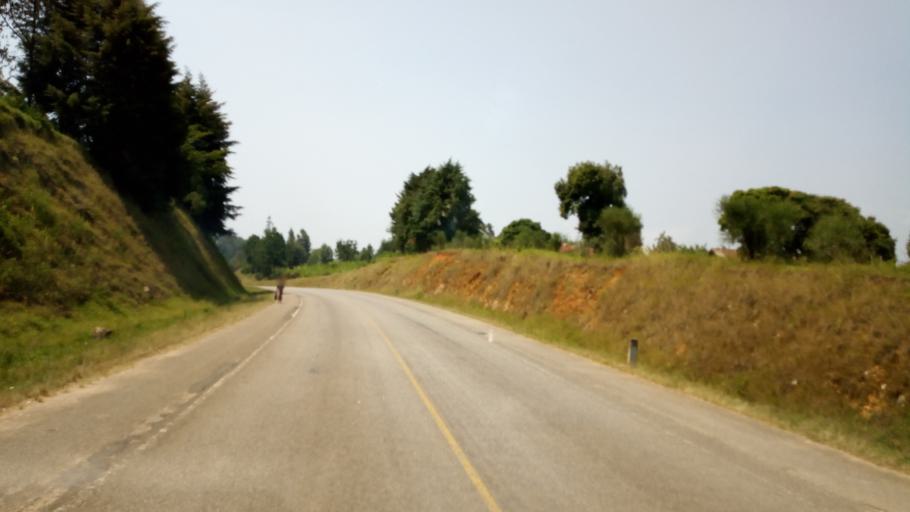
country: UG
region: Western Region
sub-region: Ntungamo District
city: Ntungamo
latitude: -0.8176
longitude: 30.1562
